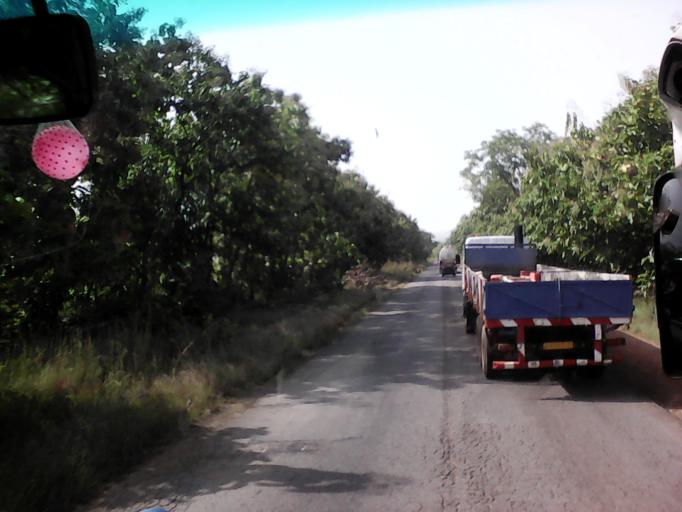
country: TG
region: Centrale
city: Sokode
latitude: 9.0906
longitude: 1.1367
